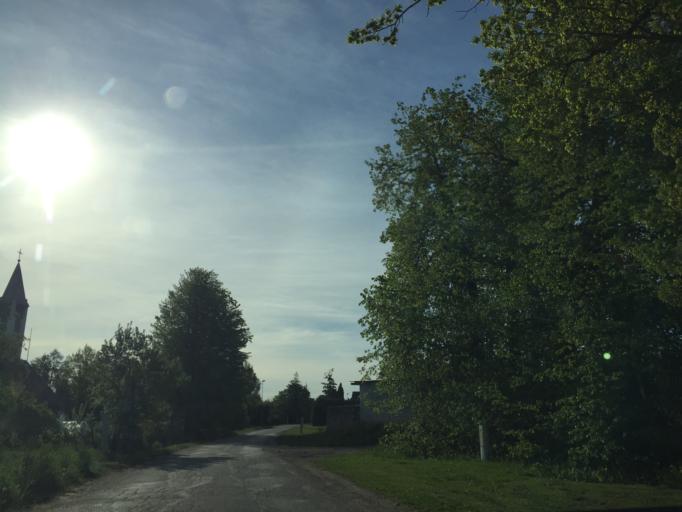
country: LV
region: Lecava
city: Iecava
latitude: 56.6022
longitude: 24.2085
